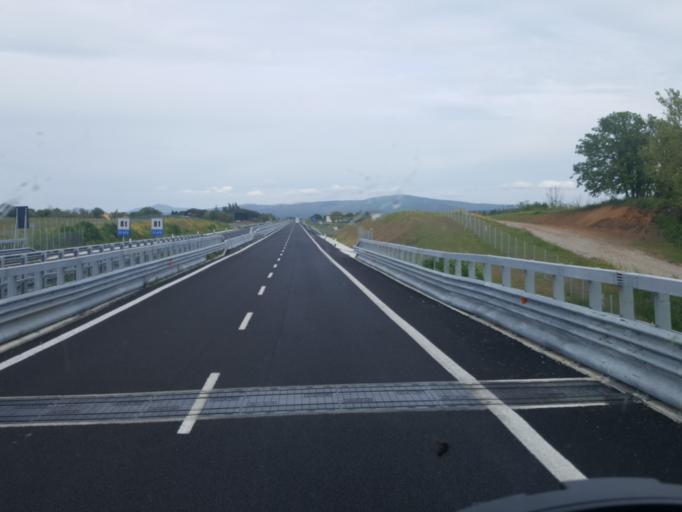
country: IT
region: Latium
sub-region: Provincia di Viterbo
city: Blera
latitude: 42.2980
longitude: 11.9665
